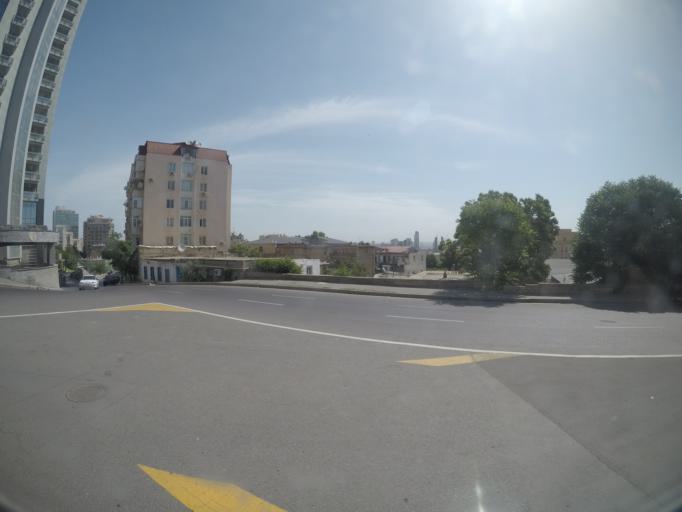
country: AZ
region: Baki
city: Badamdar
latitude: 40.3652
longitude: 49.8258
